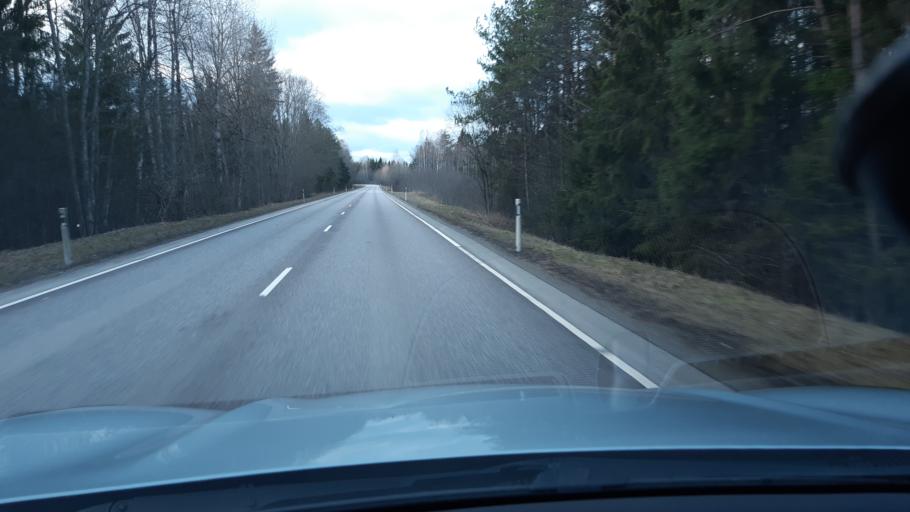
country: EE
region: Raplamaa
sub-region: Kehtna vald
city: Kehtna
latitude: 58.8834
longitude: 24.9739
